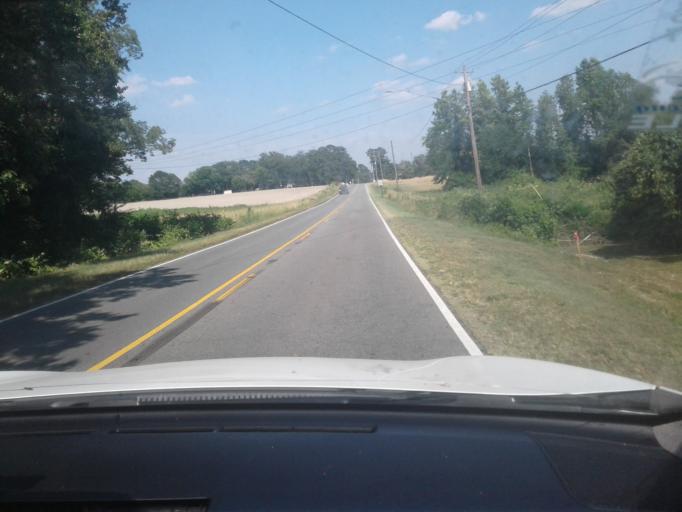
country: US
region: North Carolina
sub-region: Johnston County
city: Benson
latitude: 35.3874
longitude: -78.5630
